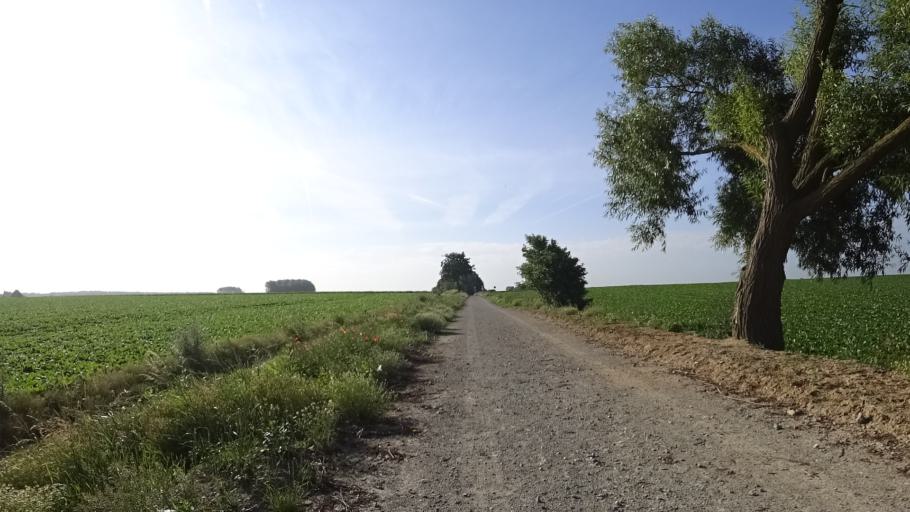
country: BE
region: Wallonia
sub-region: Province du Brabant Wallon
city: Walhain-Saint-Paul
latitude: 50.6107
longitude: 4.7117
